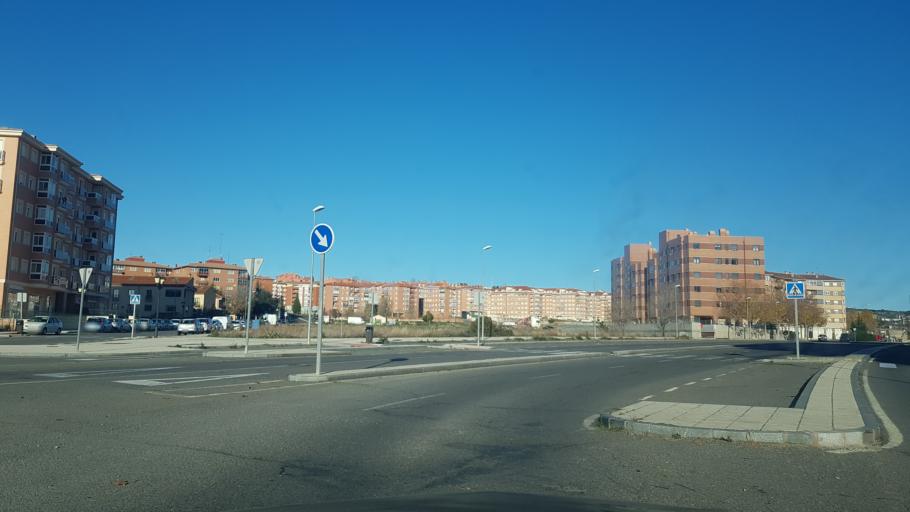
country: ES
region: Castille and Leon
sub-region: Provincia de Avila
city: Avila
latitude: 40.6442
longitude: -4.6840
